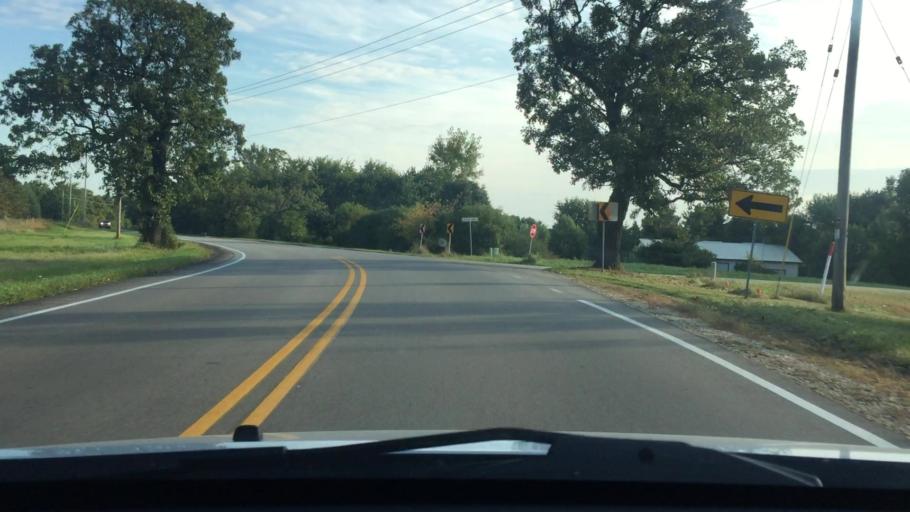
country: US
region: Wisconsin
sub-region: Waukesha County
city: Wales
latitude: 42.9777
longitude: -88.3946
